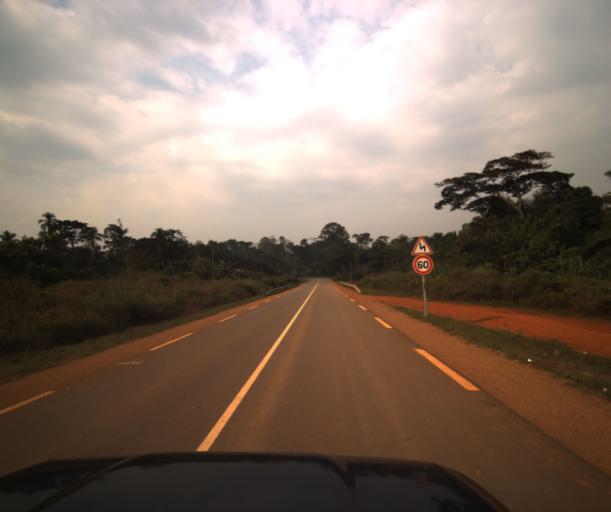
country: CM
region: Centre
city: Mbankomo
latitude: 3.7746
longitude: 11.4162
